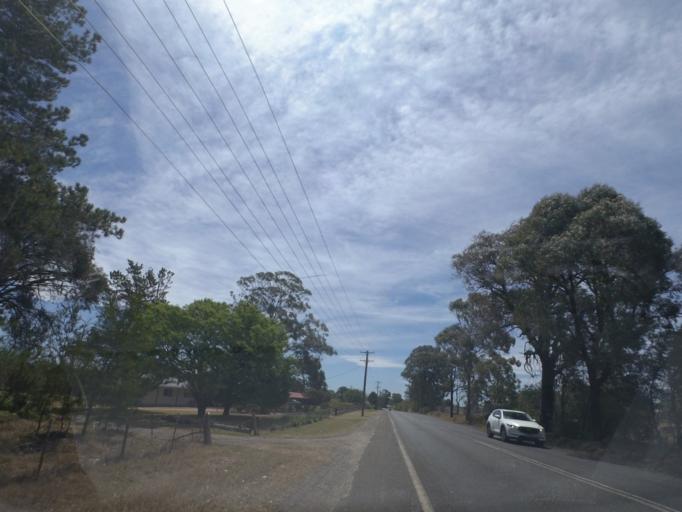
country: AU
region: New South Wales
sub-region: Wollondilly
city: Buxton
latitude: -34.3023
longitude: 150.5891
